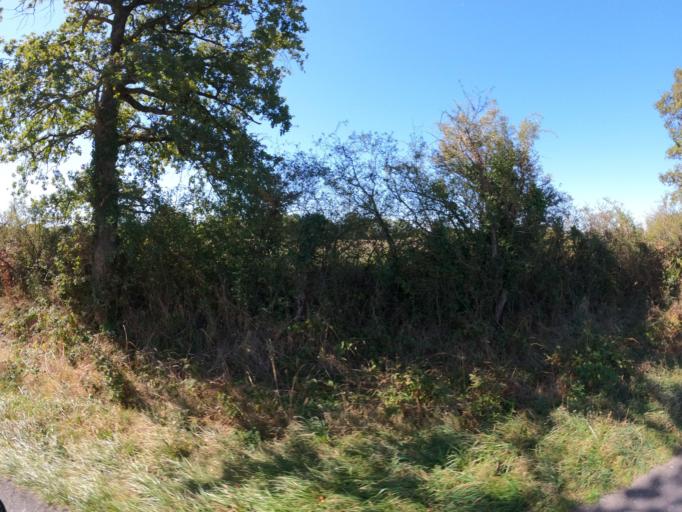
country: FR
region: Poitou-Charentes
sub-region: Departement de la Vienne
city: Lathus-Saint-Remy
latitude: 46.3096
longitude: 0.9814
